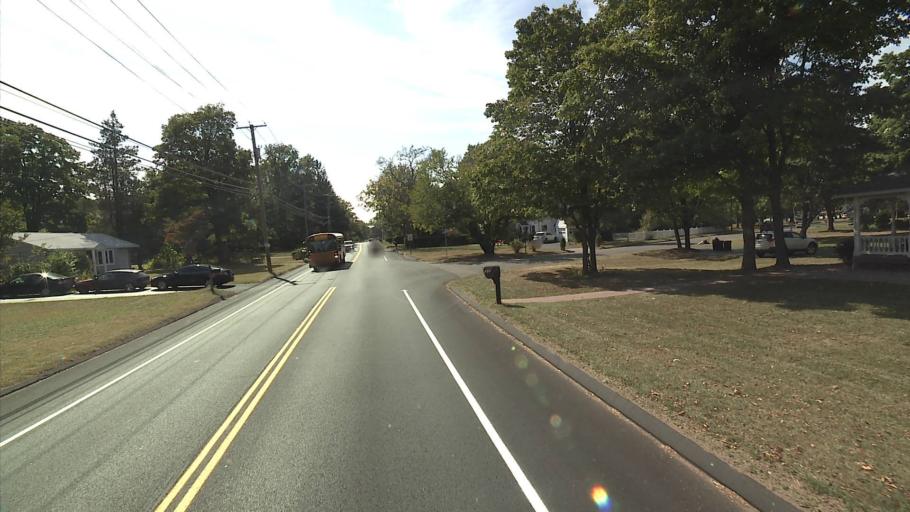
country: US
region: Connecticut
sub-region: New Haven County
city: North Haven
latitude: 41.3596
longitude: -72.8562
